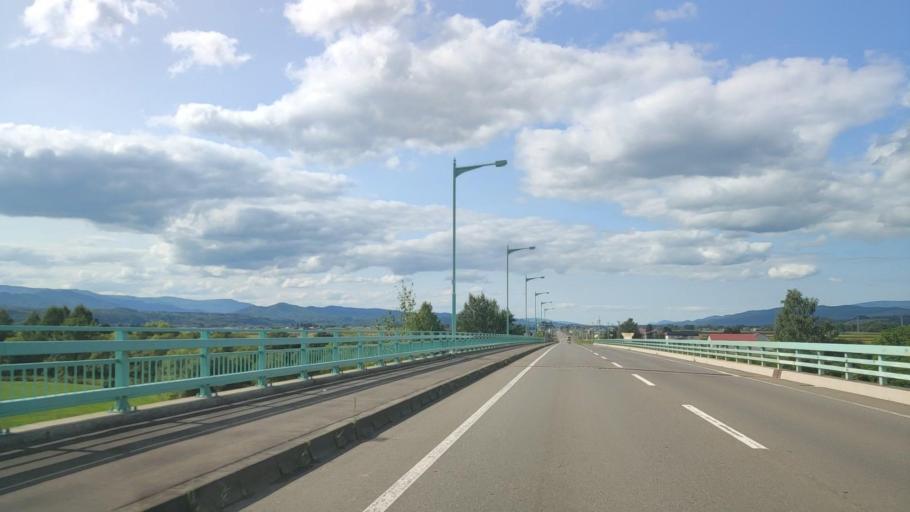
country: JP
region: Hokkaido
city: Nayoro
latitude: 44.4563
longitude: 142.3586
